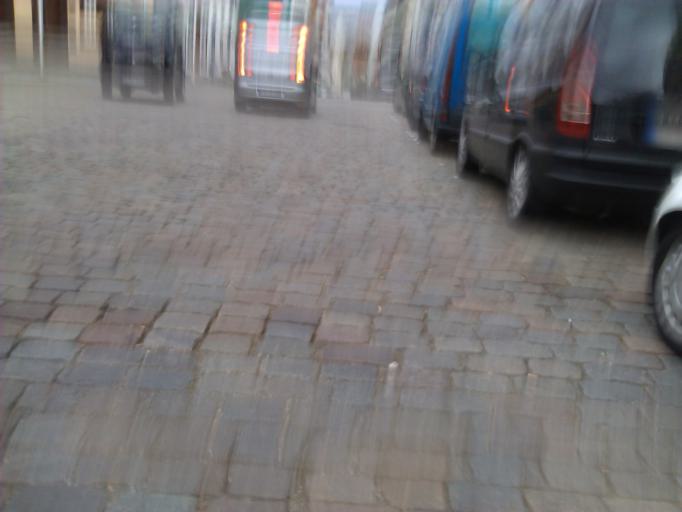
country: DE
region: Baden-Wuerttemberg
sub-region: Regierungsbezirk Stuttgart
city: Nurtingen
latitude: 48.6260
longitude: 9.3374
